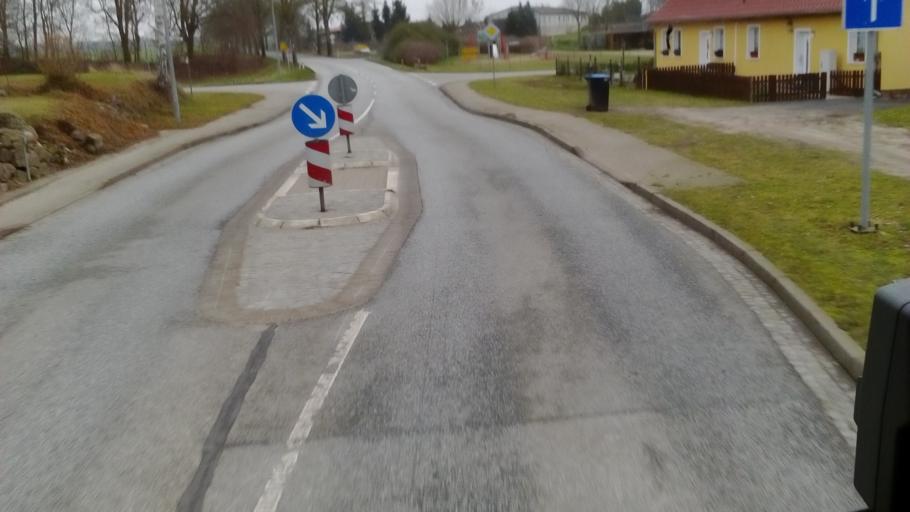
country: DE
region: Brandenburg
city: Pritzwalk
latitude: 53.1391
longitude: 12.2408
